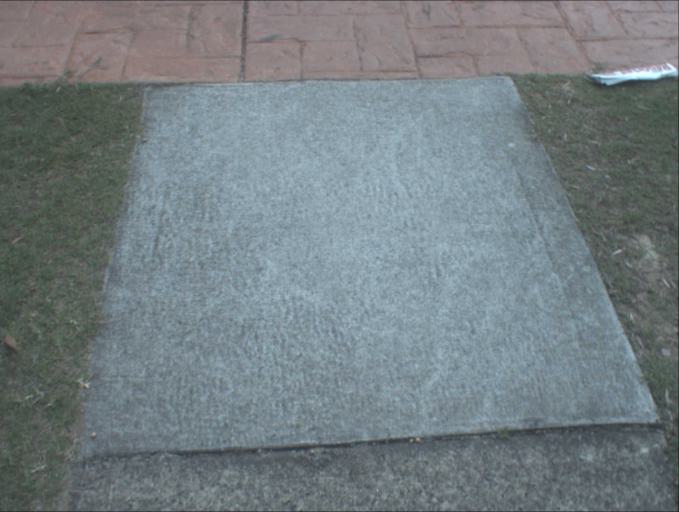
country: AU
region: Queensland
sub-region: Logan
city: Park Ridge South
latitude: -27.6777
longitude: 153.0477
